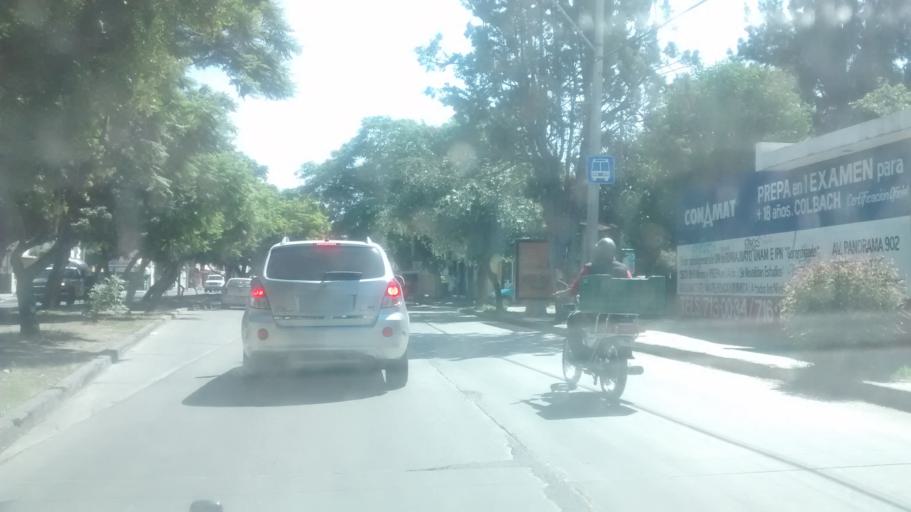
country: MX
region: Guanajuato
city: Leon
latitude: 21.1013
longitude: -101.6502
